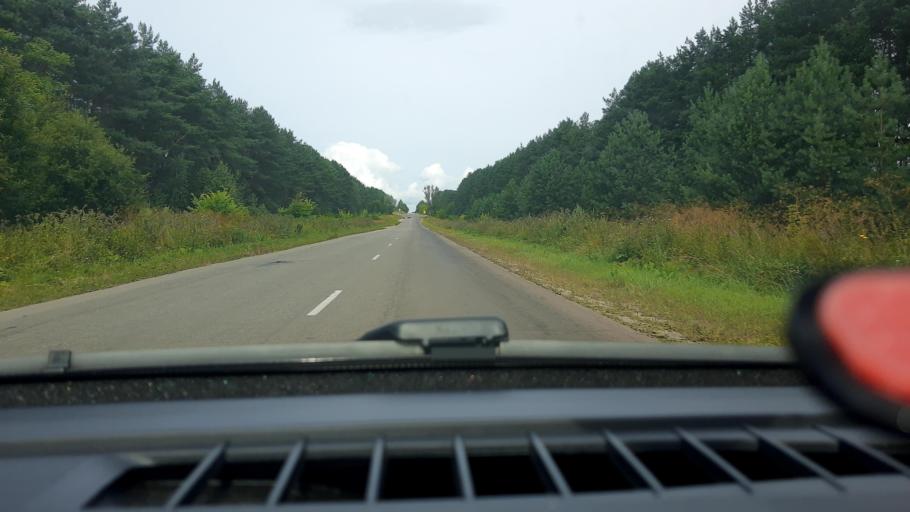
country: RU
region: Nizjnij Novgorod
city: Bogorodsk
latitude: 56.0851
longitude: 43.5670
